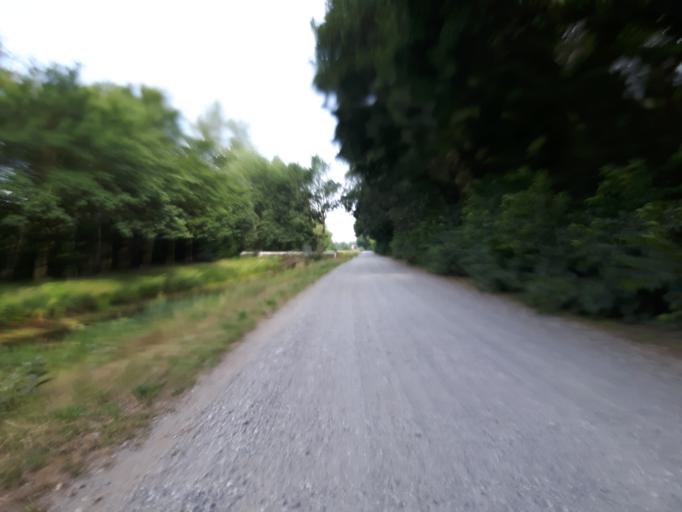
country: DE
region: Lower Saxony
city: Delmenhorst
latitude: 53.0833
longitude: 8.6303
